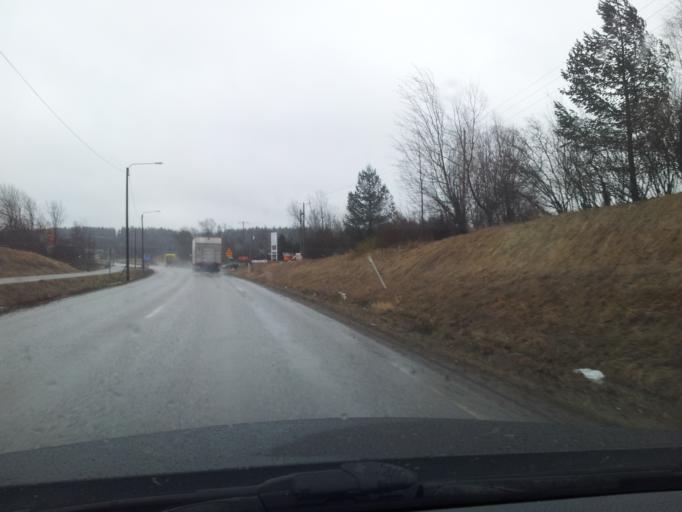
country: FI
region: Uusimaa
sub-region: Helsinki
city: Kirkkonummi
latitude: 60.1538
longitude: 24.5359
